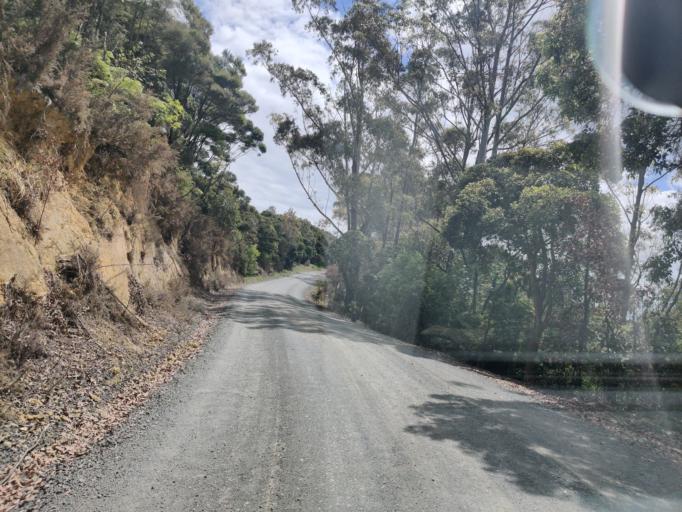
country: NZ
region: Northland
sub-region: Far North District
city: Paihia
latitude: -35.2597
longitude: 174.0573
